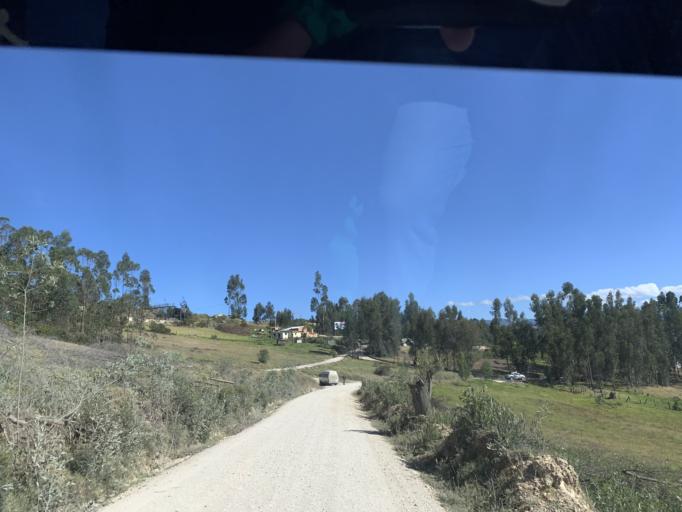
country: CO
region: Boyaca
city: Tuta
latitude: 5.7098
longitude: -73.1537
